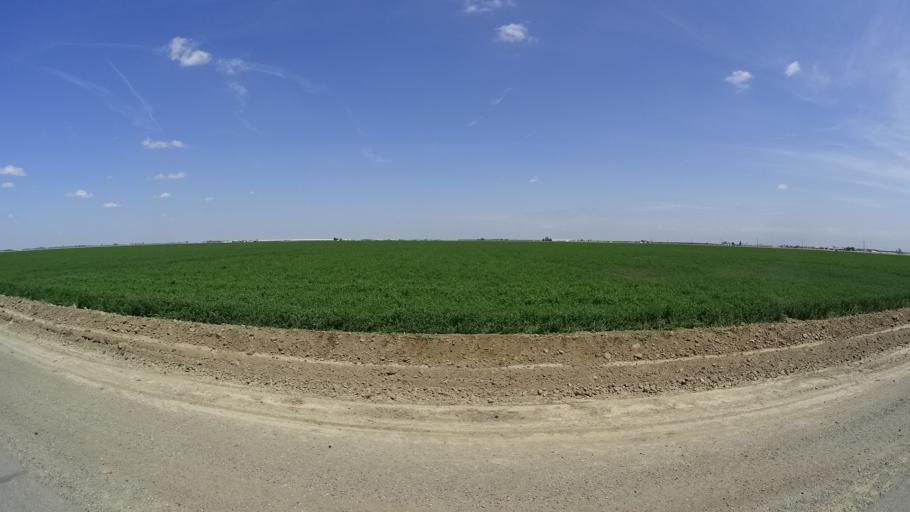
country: US
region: California
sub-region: Tulare County
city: Goshen
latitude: 36.2981
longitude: -119.5060
